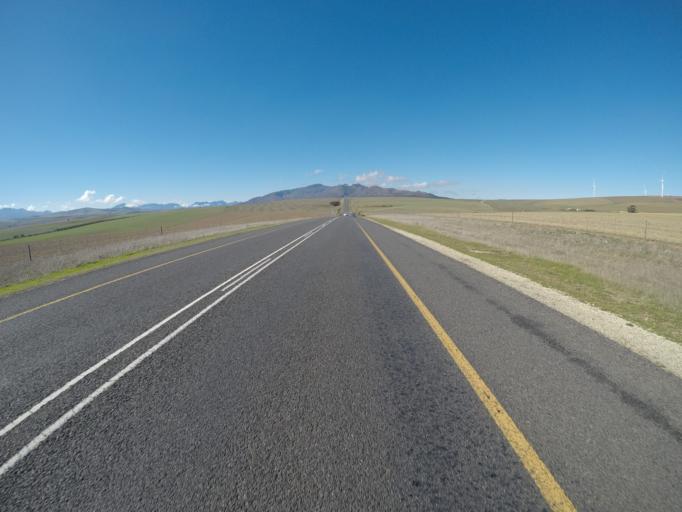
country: ZA
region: Western Cape
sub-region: Overberg District Municipality
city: Caledon
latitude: -34.2114
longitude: 19.3669
